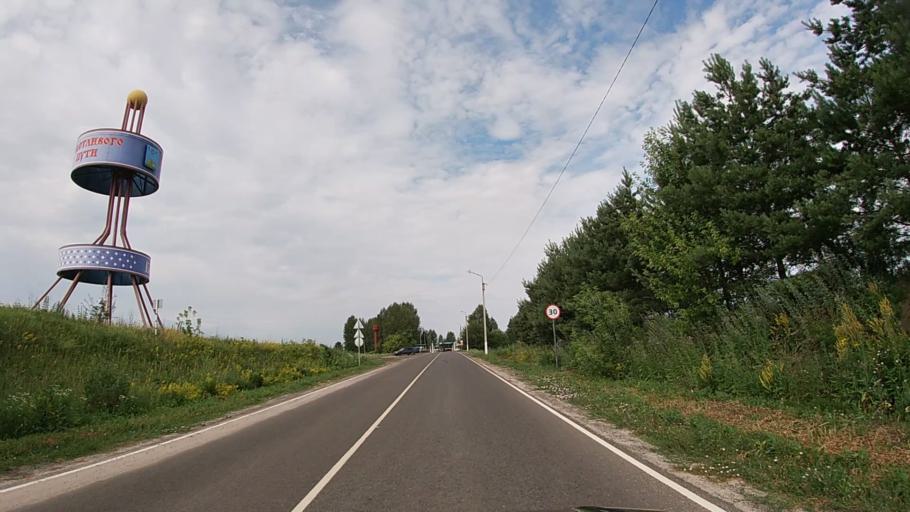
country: UA
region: Sumy
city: Krasnopillya
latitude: 50.8140
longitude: 35.4195
